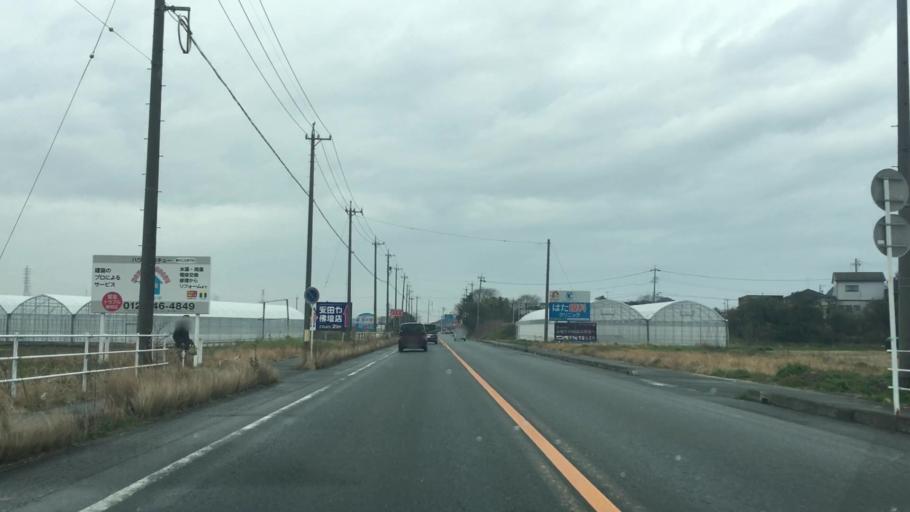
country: JP
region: Aichi
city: Toyohashi
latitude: 34.7149
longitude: 137.3918
